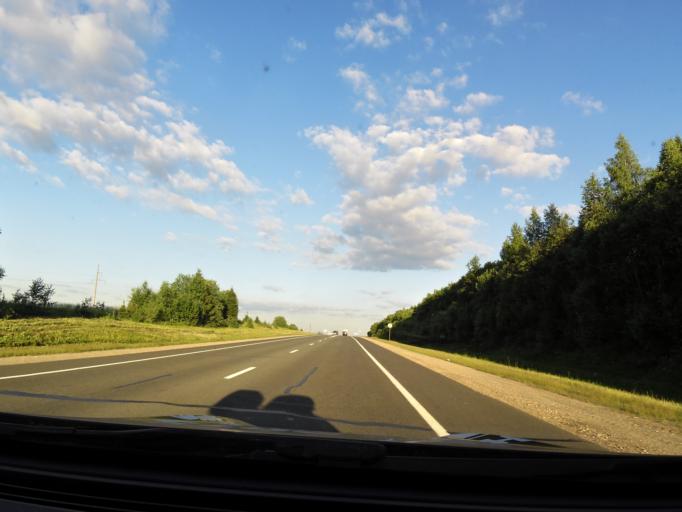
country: RU
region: Vologda
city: Vologda
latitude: 59.0639
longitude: 40.0491
